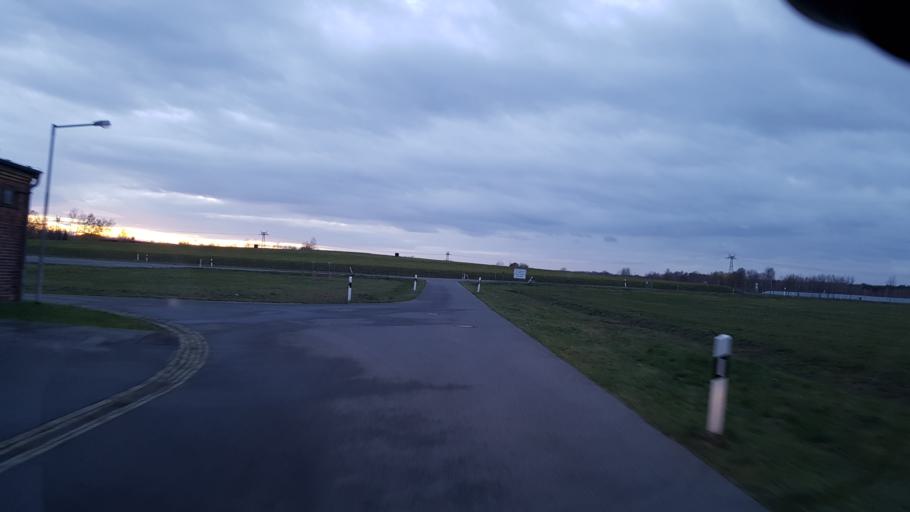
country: DE
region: Brandenburg
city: Lauchhammer
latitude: 51.4872
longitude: 13.7300
